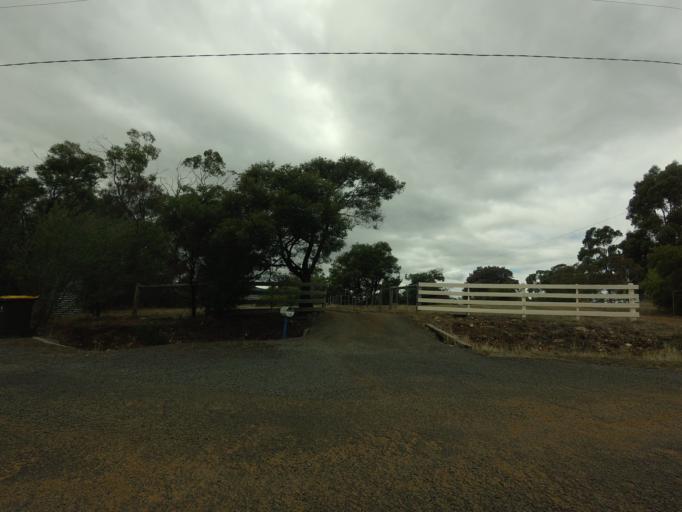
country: AU
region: Tasmania
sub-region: Clarence
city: Cambridge
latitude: -42.7816
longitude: 147.4092
